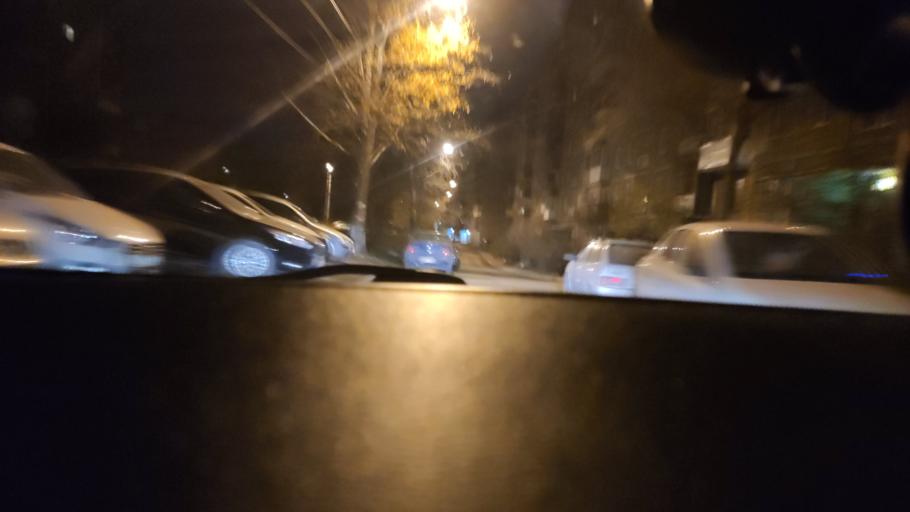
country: RU
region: Perm
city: Perm
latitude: 57.9781
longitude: 56.2213
